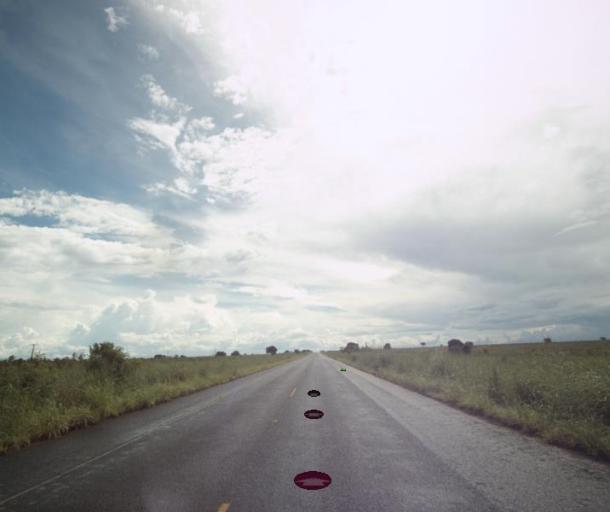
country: BR
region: Goias
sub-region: Sao Miguel Do Araguaia
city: Sao Miguel do Araguaia
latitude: -13.2953
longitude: -50.3639
